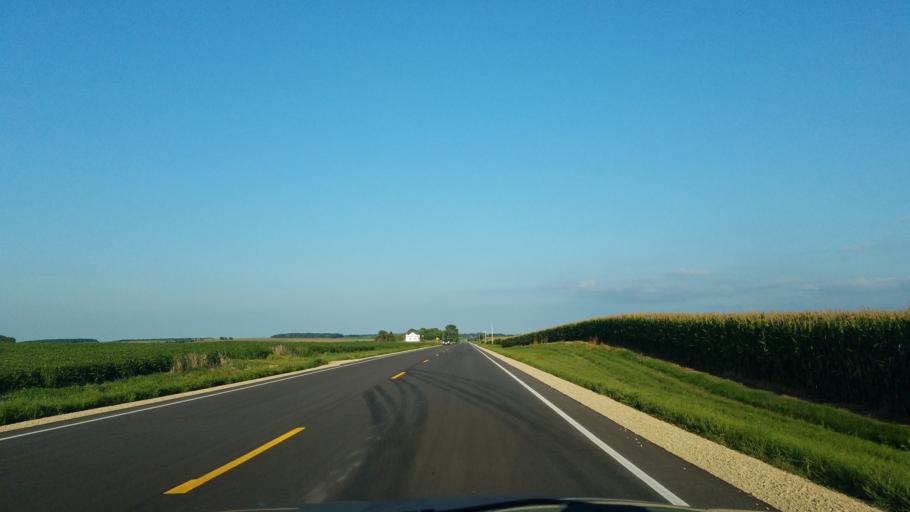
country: US
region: Wisconsin
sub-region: Saint Croix County
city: Hammond
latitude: 45.0791
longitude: -92.4120
